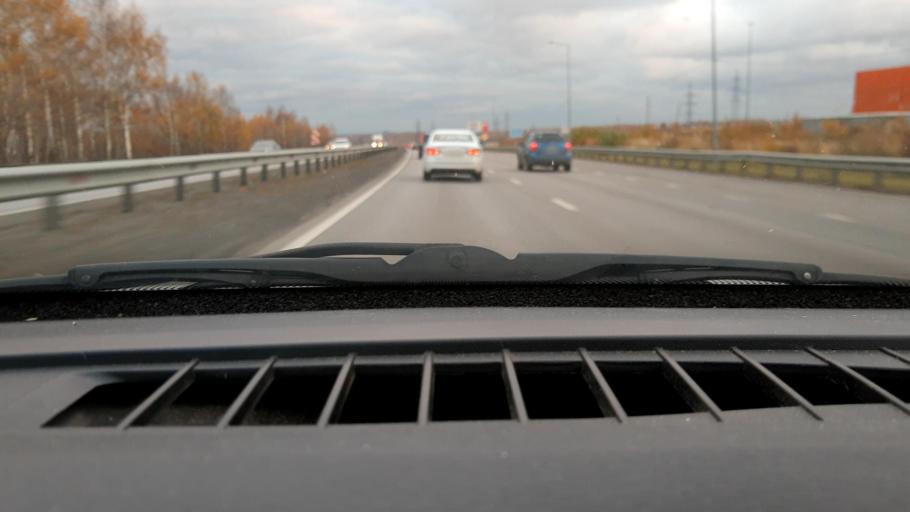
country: RU
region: Nizjnij Novgorod
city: Afonino
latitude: 56.2345
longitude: 44.0301
